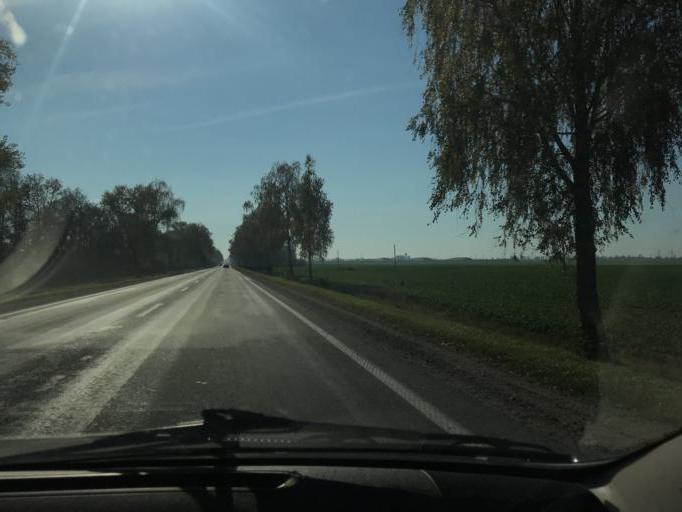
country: BY
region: Minsk
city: Salihorsk
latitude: 52.8209
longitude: 27.4654
